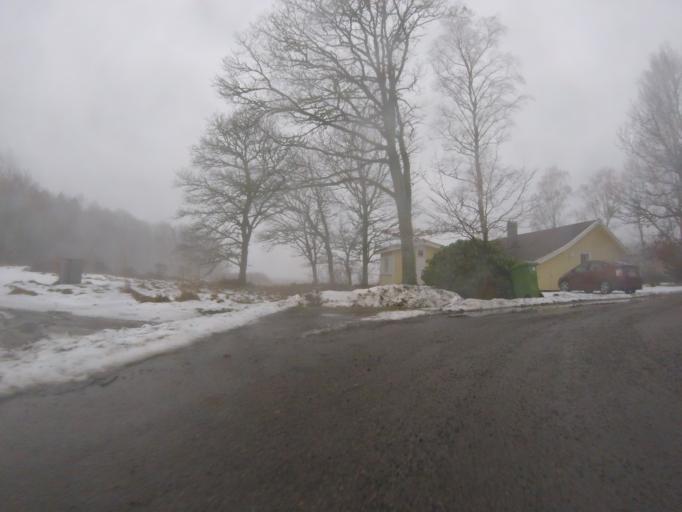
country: SE
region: Halland
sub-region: Varbergs Kommun
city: Varberg
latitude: 57.1943
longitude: 12.2145
